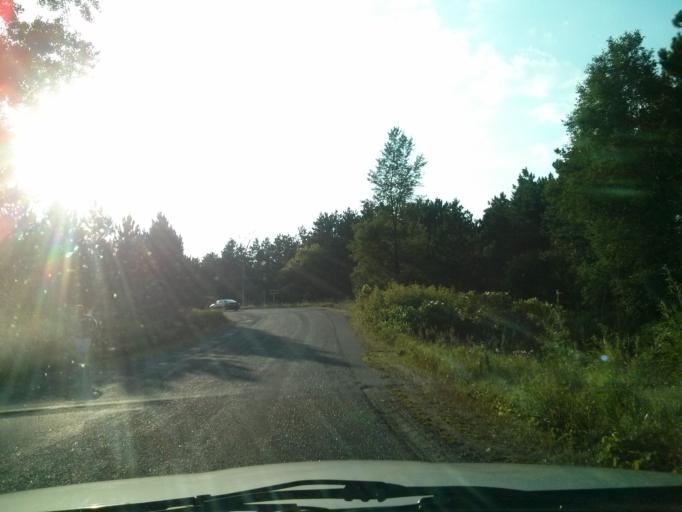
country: US
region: Wisconsin
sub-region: Saint Croix County
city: North Hudson
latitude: 45.0115
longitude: -92.6849
